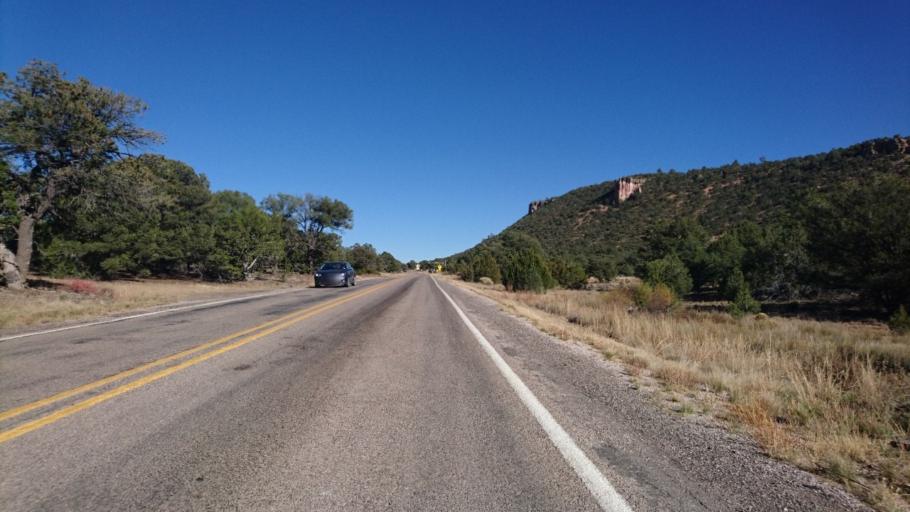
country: US
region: New Mexico
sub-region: McKinley County
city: Thoreau
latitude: 35.0437
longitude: -108.3255
